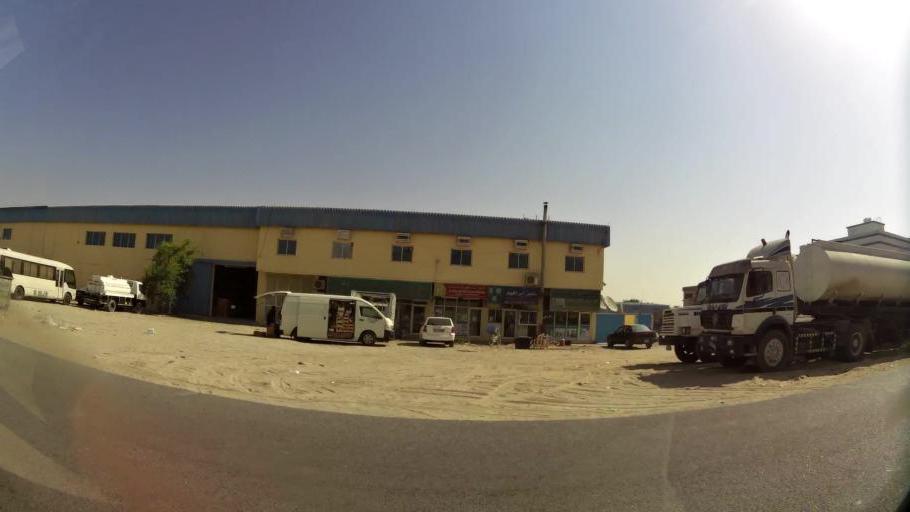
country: AE
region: Ajman
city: Ajman
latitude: 25.4324
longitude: 55.5451
